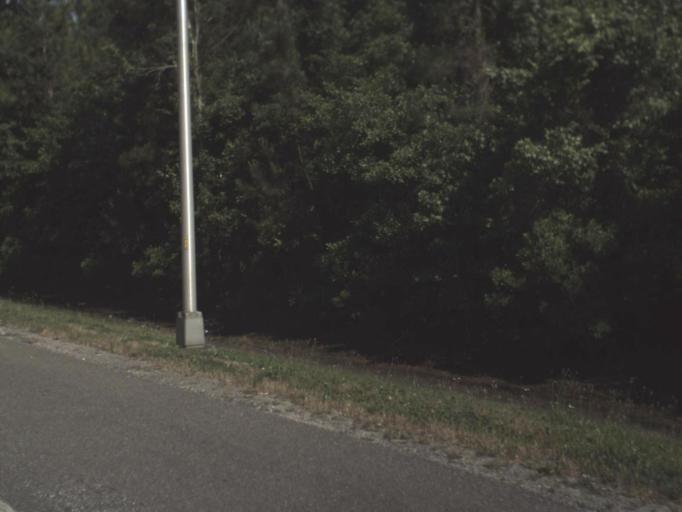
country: US
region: Florida
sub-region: Duval County
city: Jacksonville
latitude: 30.2499
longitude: -81.5681
